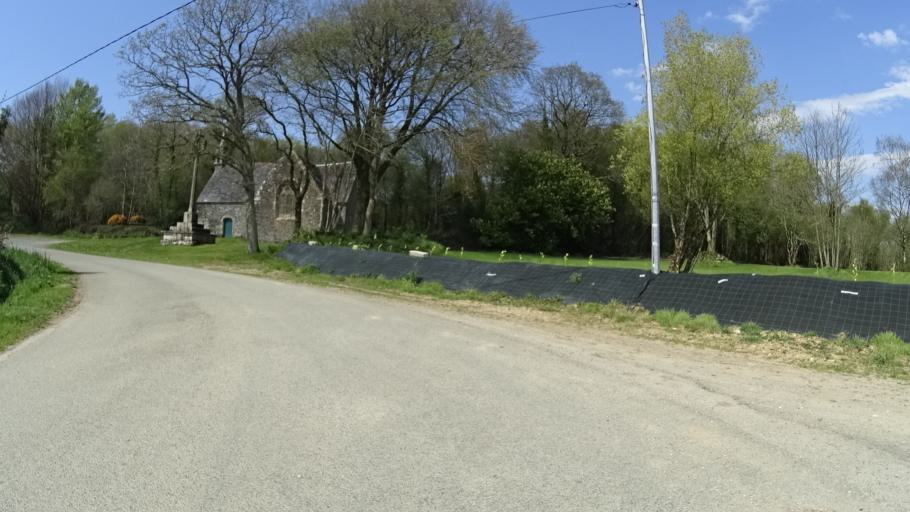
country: FR
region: Brittany
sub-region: Departement du Finistere
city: Sizun
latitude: 48.4410
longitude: -4.0990
